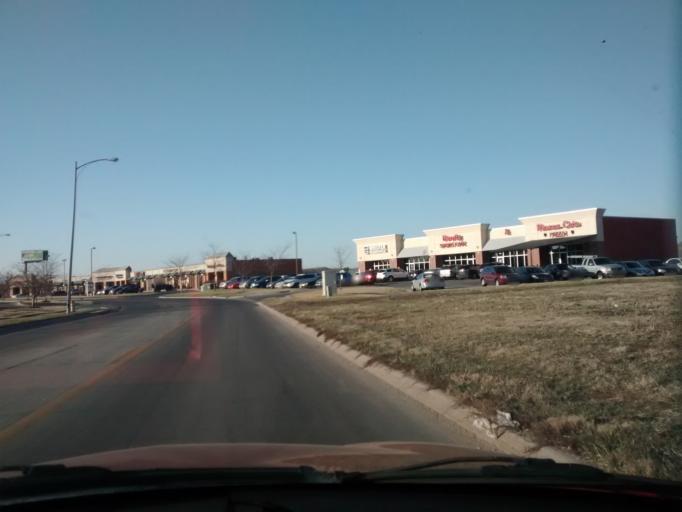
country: US
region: Nebraska
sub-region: Sarpy County
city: Offutt Air Force Base
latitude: 41.1408
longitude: -95.9653
